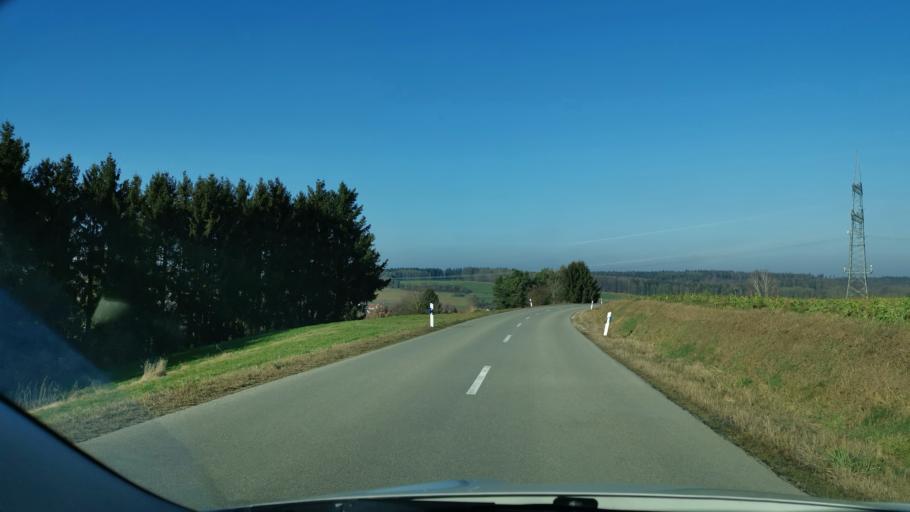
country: DE
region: Bavaria
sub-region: Swabia
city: Aindling
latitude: 48.5238
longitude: 10.9531
